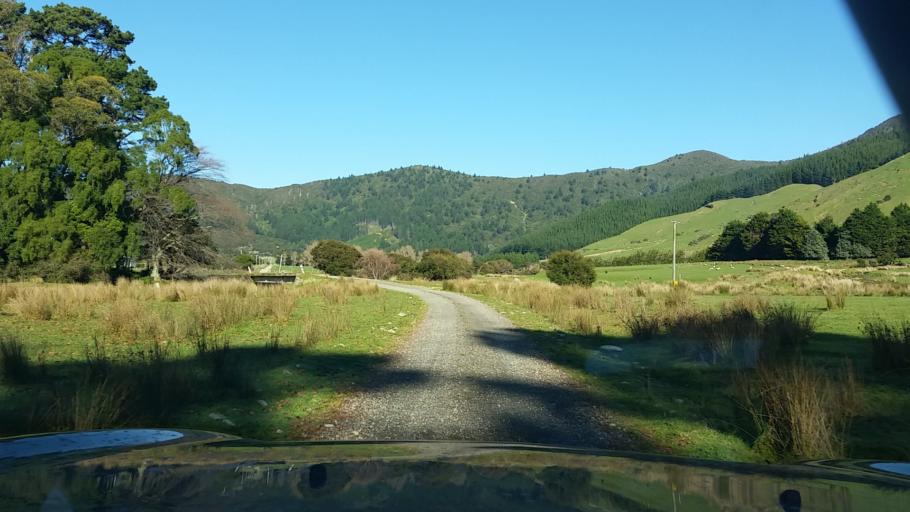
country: NZ
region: Marlborough
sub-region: Marlborough District
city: Picton
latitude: -41.1140
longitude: 174.0353
